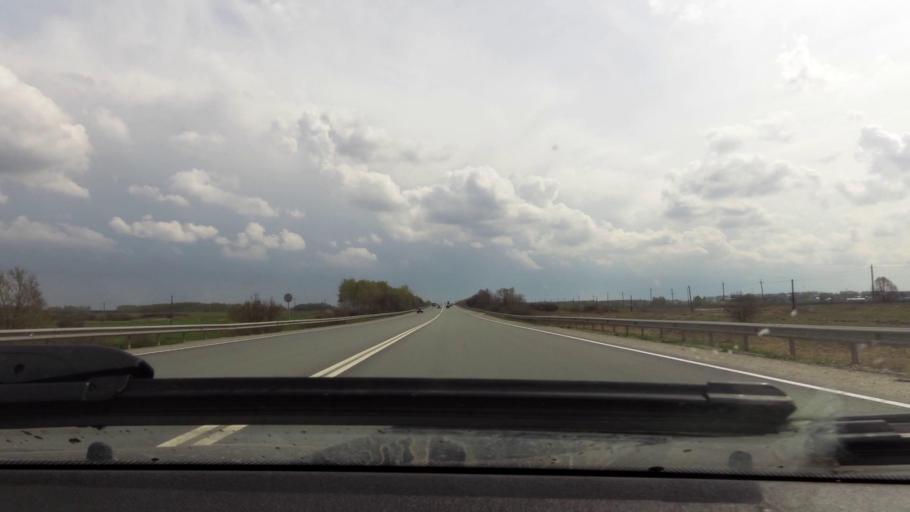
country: RU
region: Rjazan
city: Bagramovo
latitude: 54.7410
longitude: 39.4432
